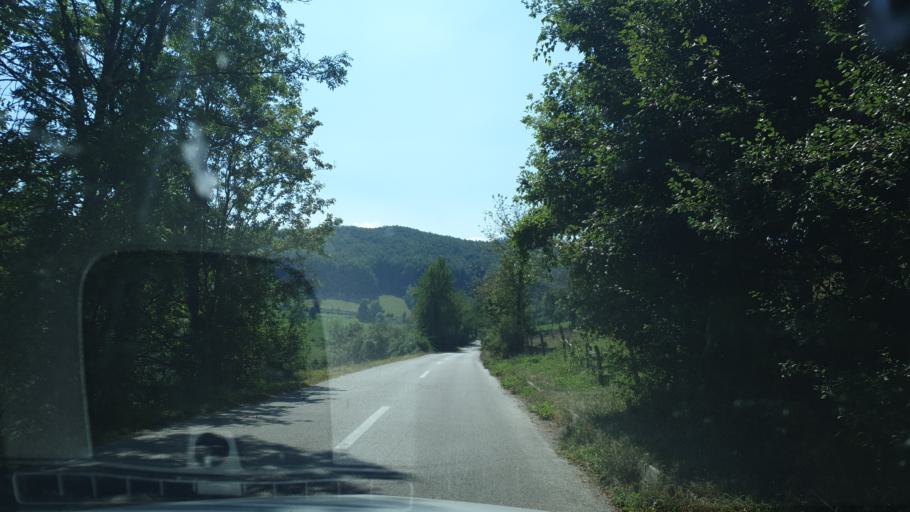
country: RS
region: Central Serbia
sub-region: Zlatiborski Okrug
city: Cajetina
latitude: 43.6849
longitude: 19.8477
